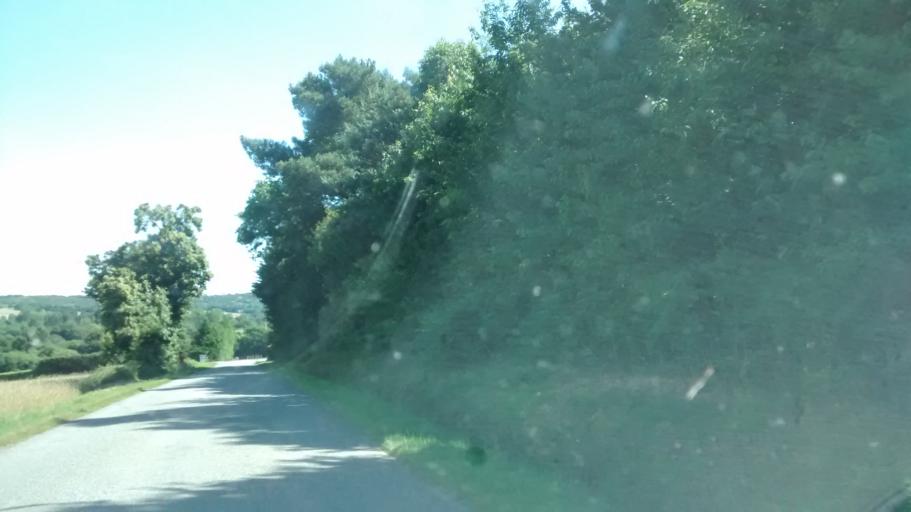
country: FR
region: Brittany
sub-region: Departement du Morbihan
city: Campeneac
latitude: 47.9963
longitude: -2.3006
